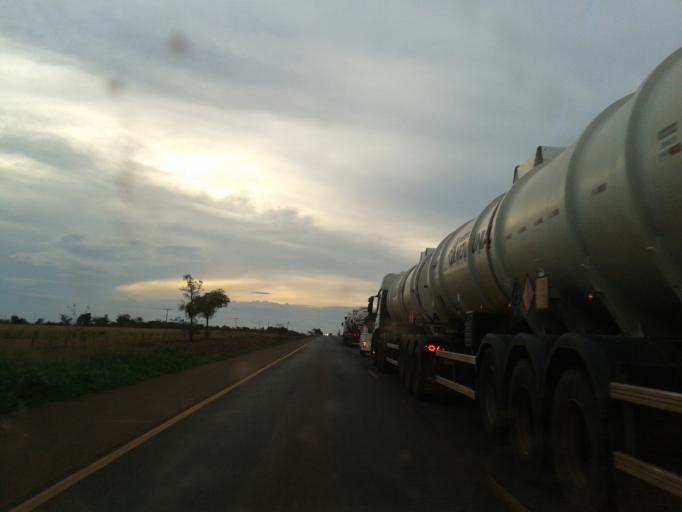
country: BR
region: Goias
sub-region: Santa Helena De Goias
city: Santa Helena de Goias
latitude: -17.9364
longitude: -50.5373
